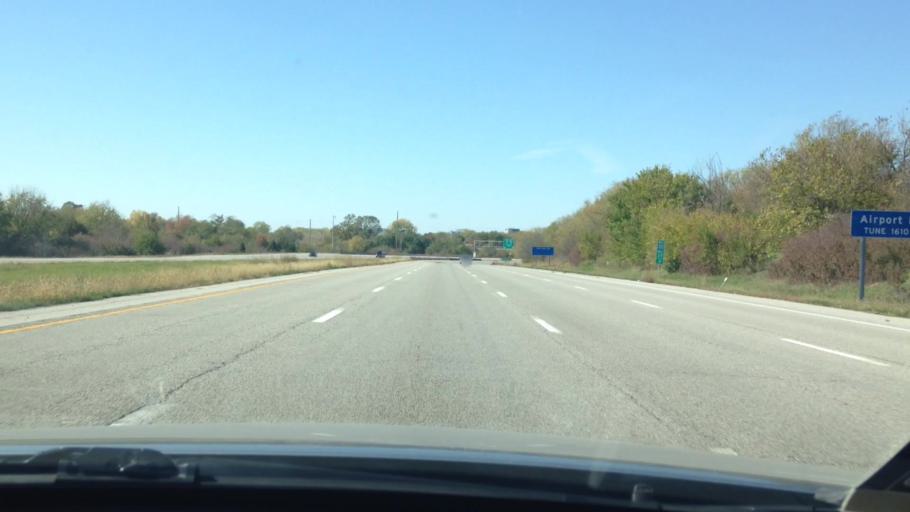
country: US
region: Missouri
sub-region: Platte County
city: Weatherby Lake
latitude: 39.3076
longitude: -94.6619
